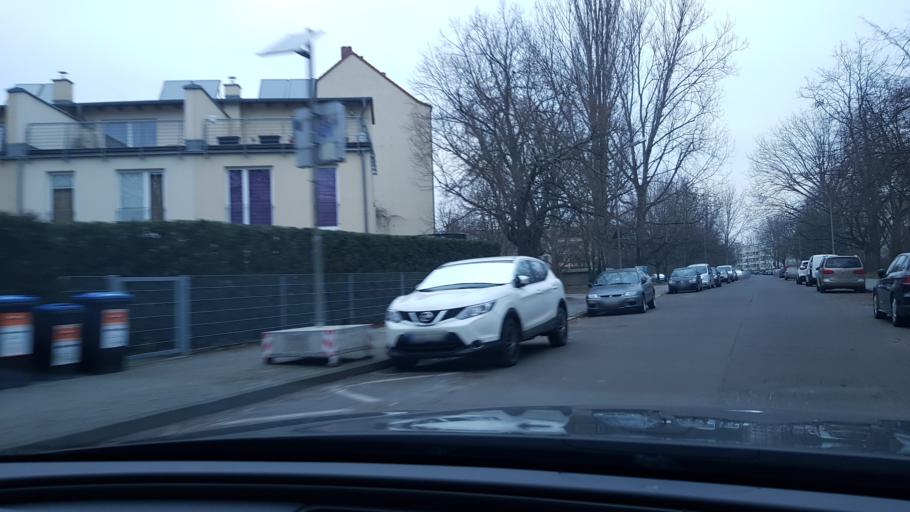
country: DE
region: Berlin
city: Grunau
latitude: 52.4238
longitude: 13.5916
